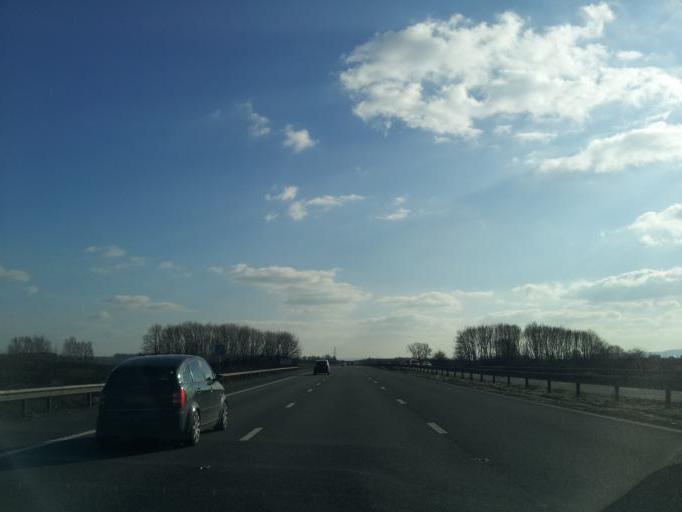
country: GB
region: England
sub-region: Somerset
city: Highbridge
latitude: 51.1953
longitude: -2.9702
